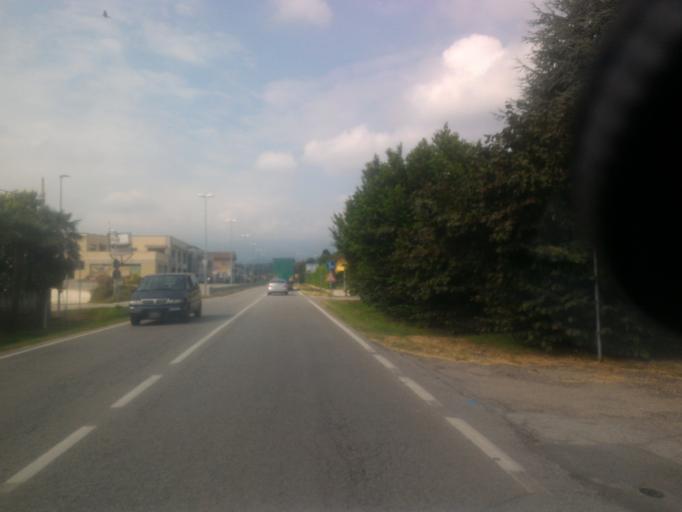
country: IT
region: Piedmont
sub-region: Provincia di Torino
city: Bricherasio
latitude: 44.8411
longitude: 7.3083
